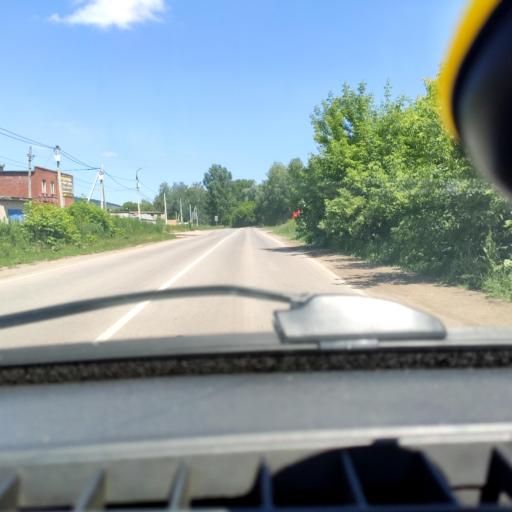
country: RU
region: Samara
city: Zhigulevsk
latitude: 53.3895
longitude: 49.5086
